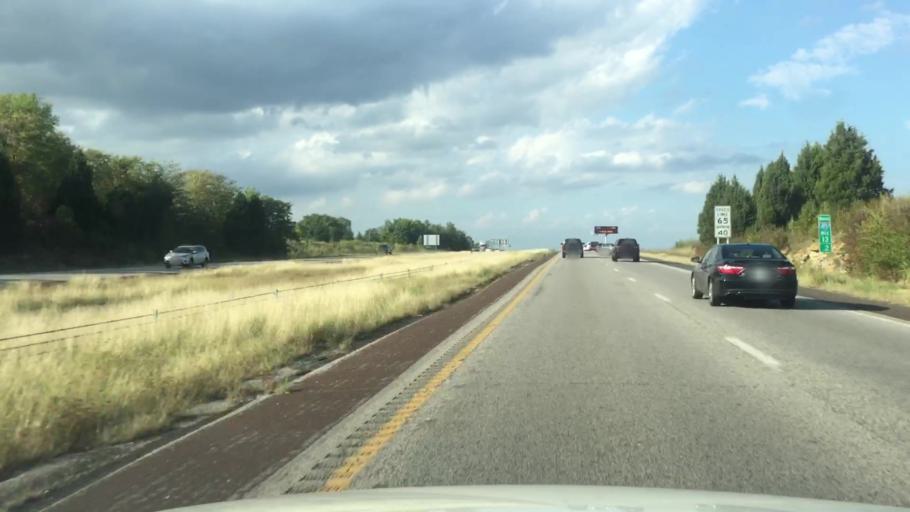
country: US
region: Missouri
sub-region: Jackson County
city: Blue Springs
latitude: 38.9912
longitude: -94.3574
